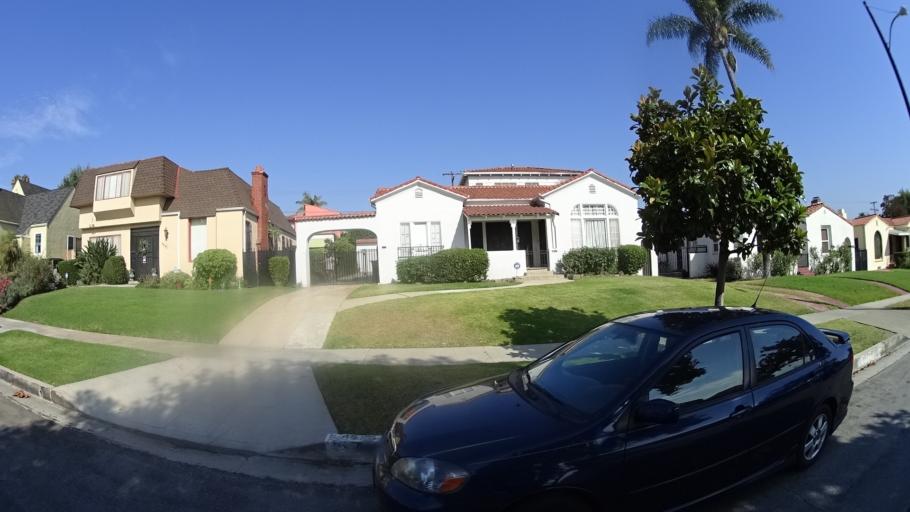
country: US
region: California
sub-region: Los Angeles County
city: View Park-Windsor Hills
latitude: 34.0016
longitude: -118.3328
